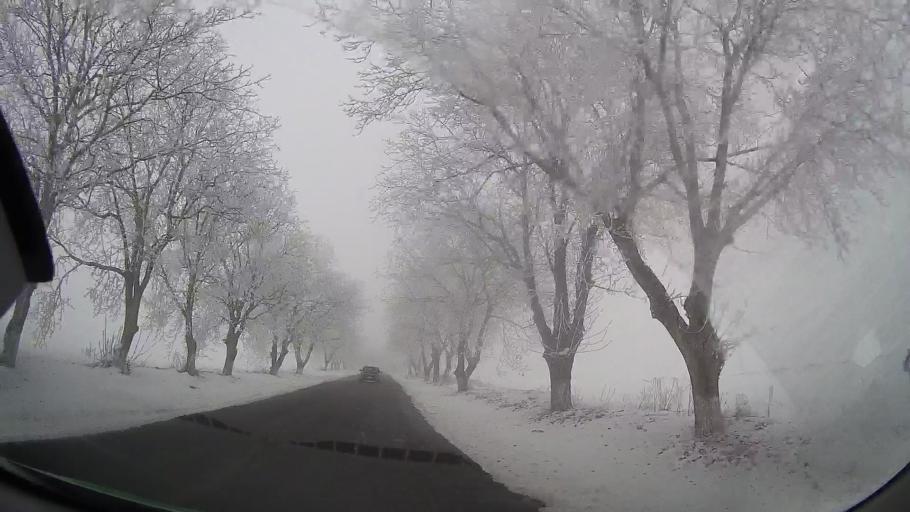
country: RO
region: Neamt
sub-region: Comuna Cordun
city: Cordun
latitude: 46.9845
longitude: 26.8644
